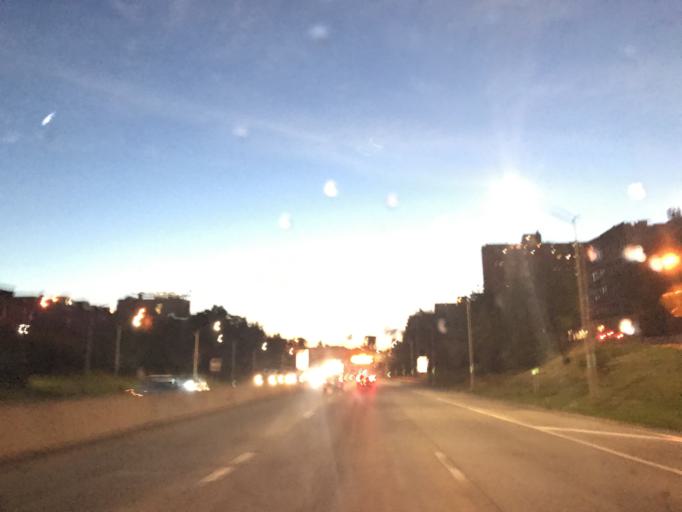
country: US
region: New York
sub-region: New York County
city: Manhattan
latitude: 40.8059
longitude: -73.9218
